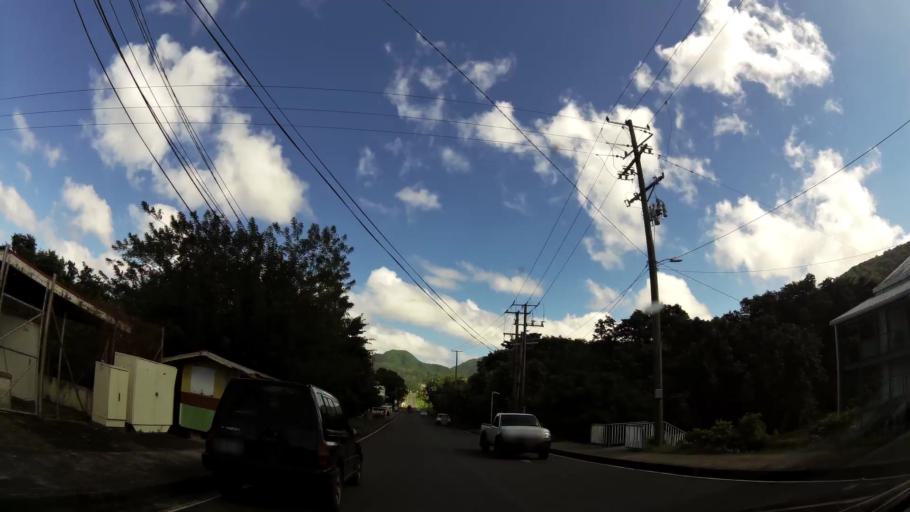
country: DM
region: Saint John
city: Portsmouth
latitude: 15.5578
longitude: -61.4574
